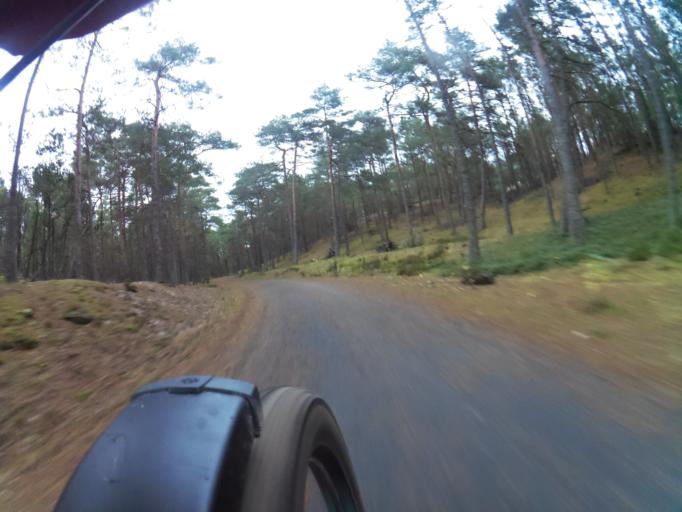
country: PL
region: Pomeranian Voivodeship
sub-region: Powiat wejherowski
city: Choczewo
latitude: 54.7850
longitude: 17.7456
